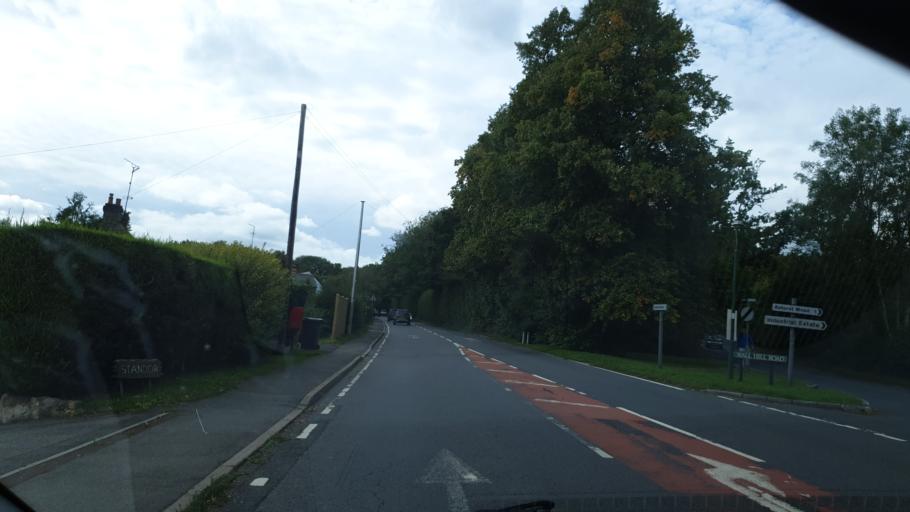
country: GB
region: England
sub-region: East Sussex
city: Forest Row
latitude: 51.1029
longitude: 0.0328
